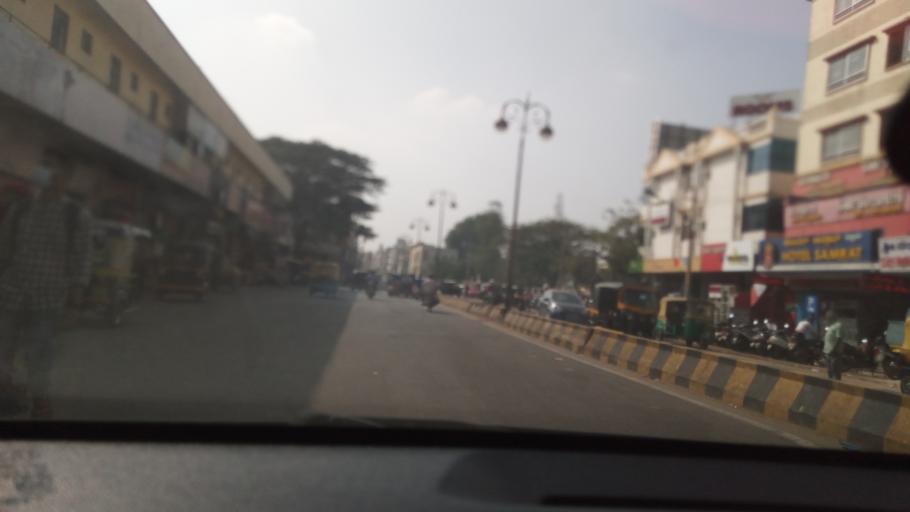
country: IN
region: Karnataka
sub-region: Mysore
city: Mysore
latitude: 12.3135
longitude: 76.6588
